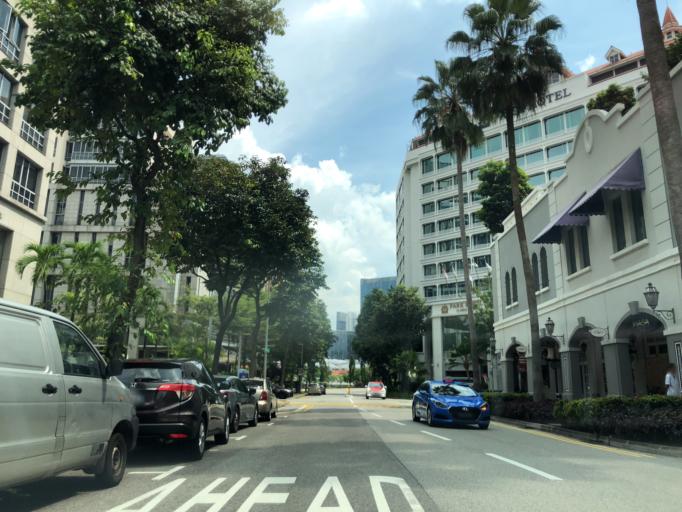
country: SG
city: Singapore
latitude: 1.2923
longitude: 103.8418
